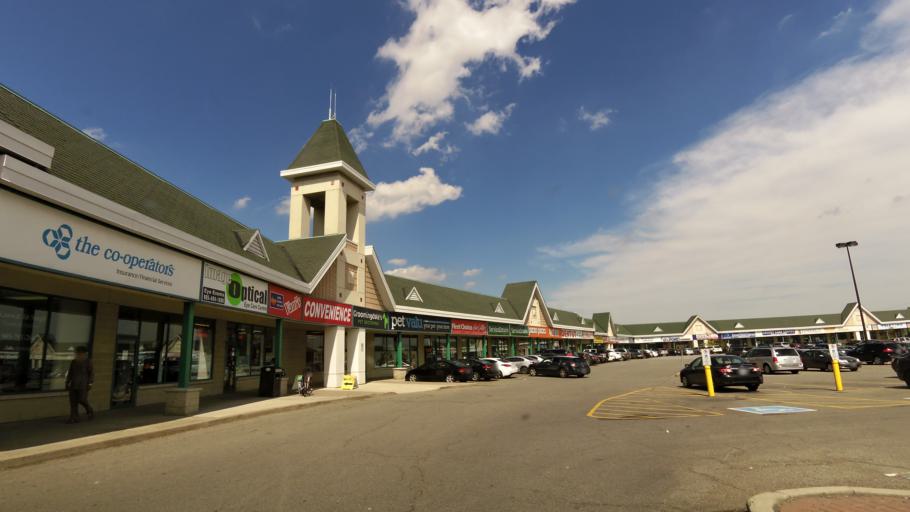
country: CA
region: Ontario
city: Brampton
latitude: 43.7603
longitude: -79.7295
